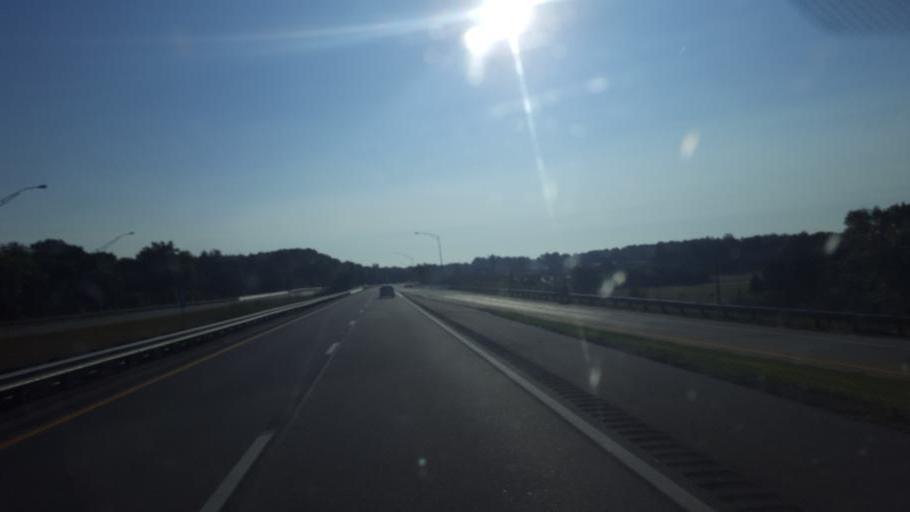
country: US
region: Ohio
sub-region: Cuyahoga County
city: Solon
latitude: 41.3948
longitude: -81.4354
